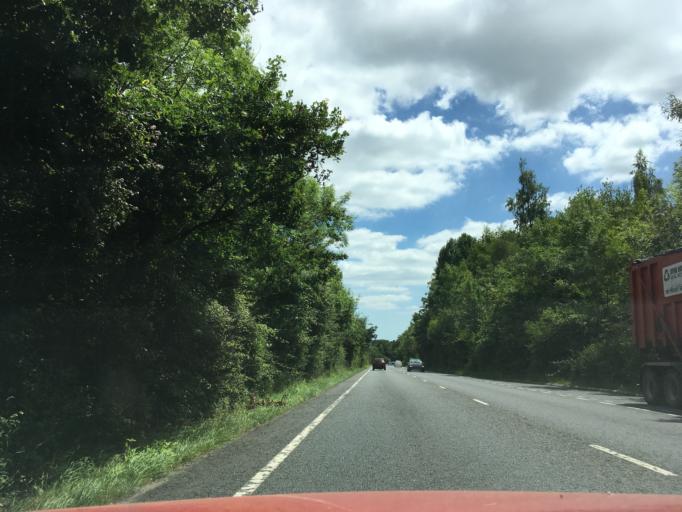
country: GB
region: England
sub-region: Hampshire
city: Eastleigh
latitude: 50.9924
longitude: -1.3536
